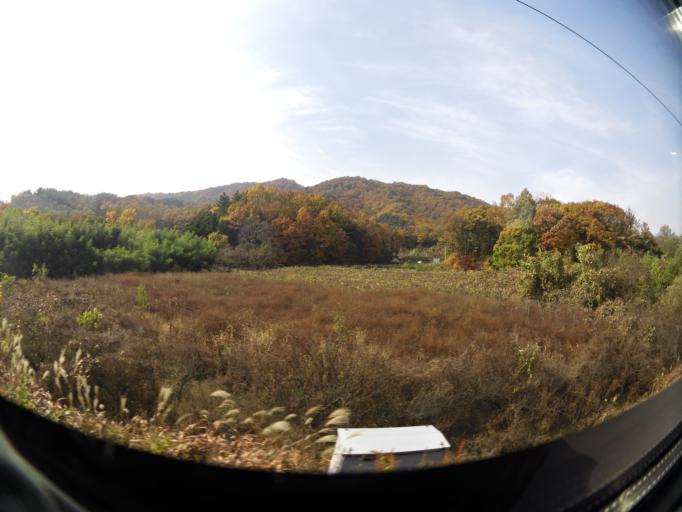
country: KR
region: Gyeongsangbuk-do
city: Gimcheon
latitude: 36.1900
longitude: 128.0065
